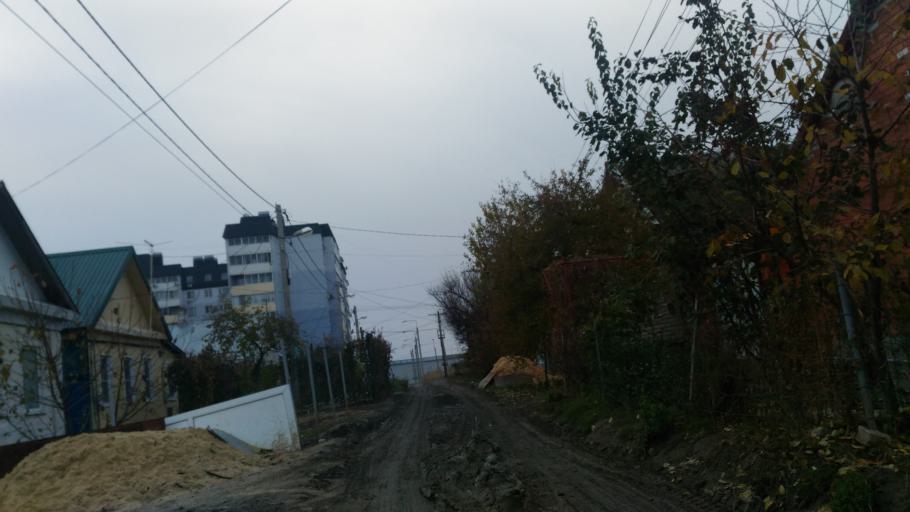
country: RU
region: Volgograd
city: Volgograd
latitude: 48.6465
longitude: 44.4297
